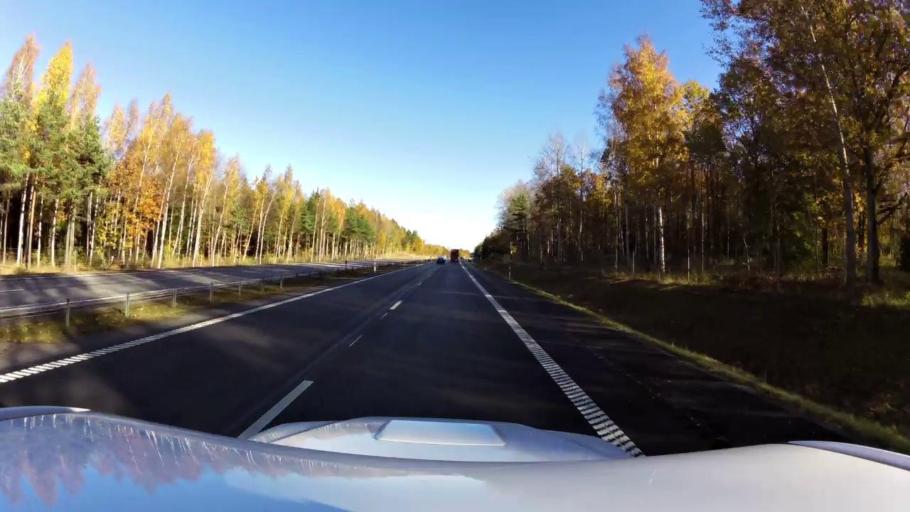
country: SE
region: OEstergoetland
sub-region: Linkopings Kommun
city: Malmslatt
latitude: 58.4222
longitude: 15.4890
